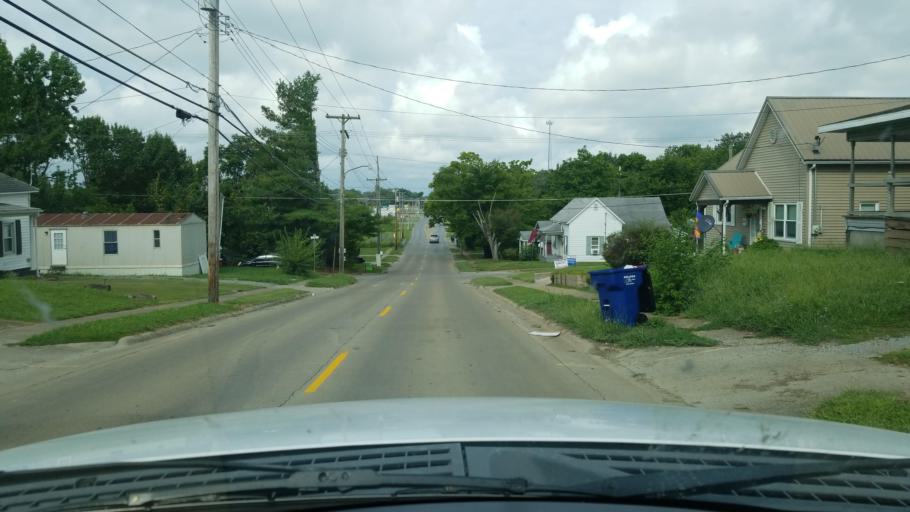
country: US
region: Illinois
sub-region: Saline County
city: Harrisburg
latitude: 37.7310
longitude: -88.5297
